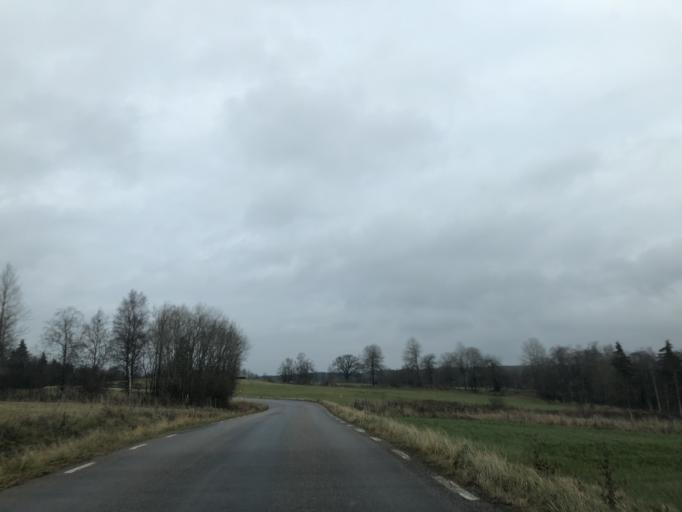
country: SE
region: Vaestra Goetaland
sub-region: Ulricehamns Kommun
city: Ulricehamn
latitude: 57.8881
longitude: 13.5117
